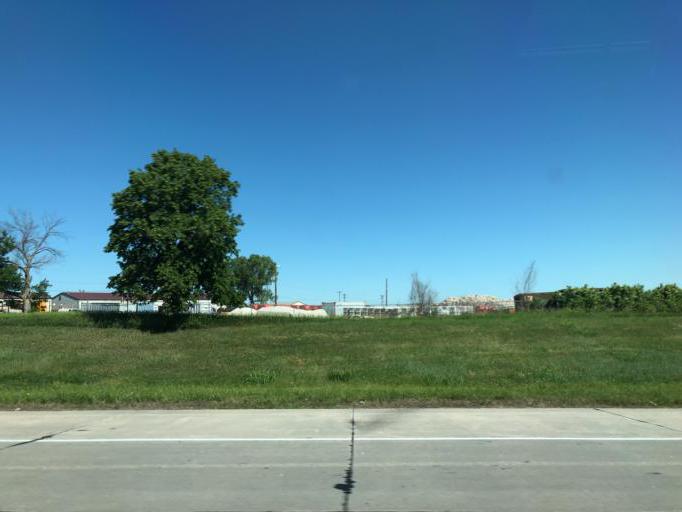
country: US
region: Nebraska
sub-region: Lancaster County
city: Lincoln
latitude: 40.8174
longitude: -96.7567
